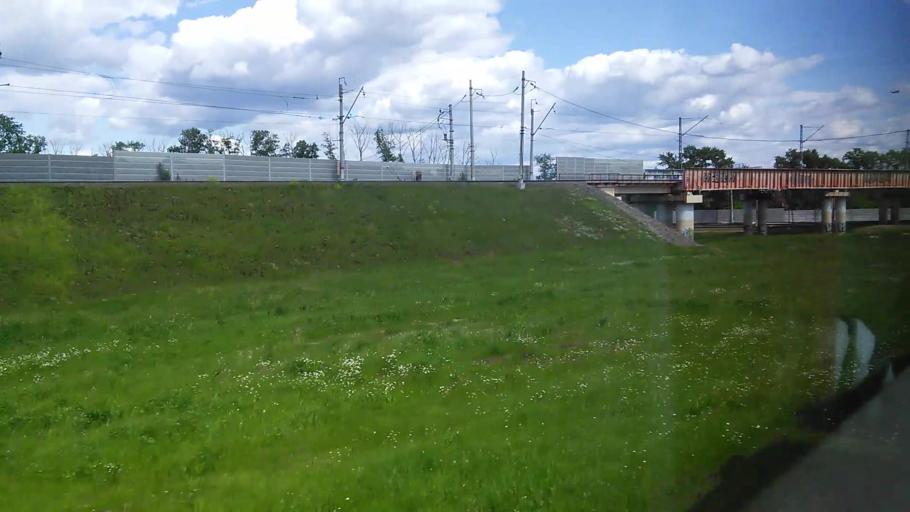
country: RU
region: Moskovskaya
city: Lobnya
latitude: 55.9983
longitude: 37.4895
